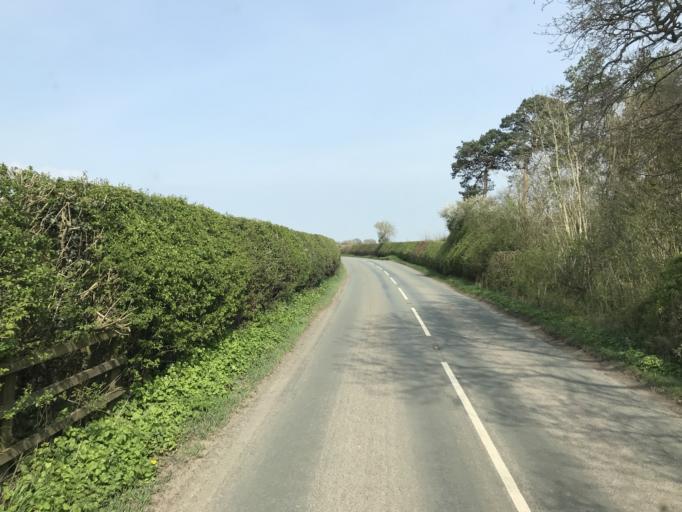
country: GB
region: England
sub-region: Cheshire West and Chester
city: Aldford
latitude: 53.1428
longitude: -2.8627
